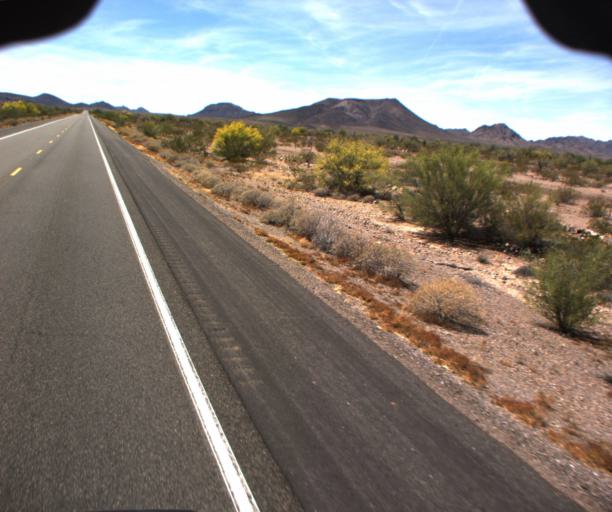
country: US
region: Arizona
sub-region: La Paz County
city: Quartzsite
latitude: 33.6721
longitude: -113.9756
